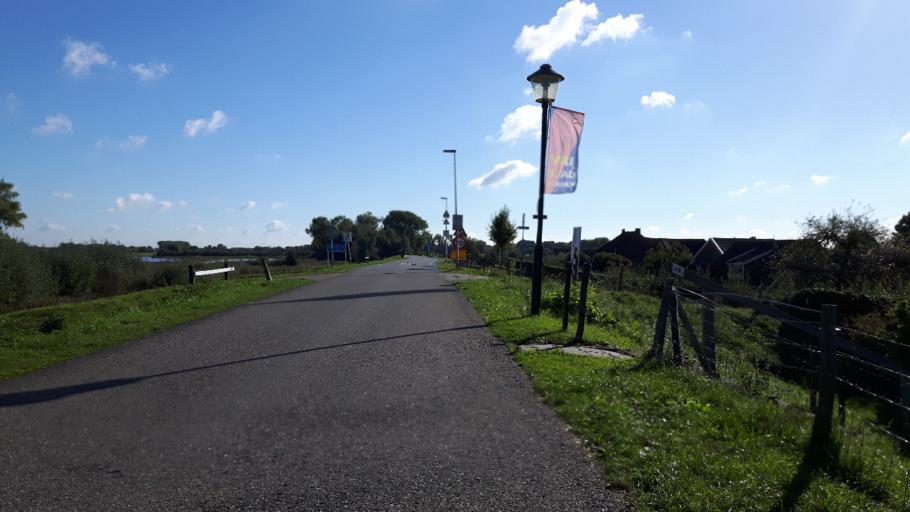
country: NL
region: Utrecht
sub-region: Gemeente Houten
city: Houten
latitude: 51.9660
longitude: 5.1585
